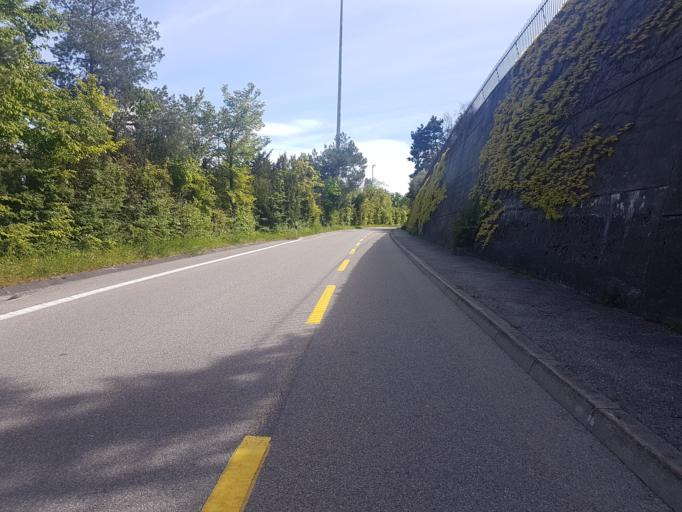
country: CH
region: Geneva
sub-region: Geneva
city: Bellevue
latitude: 46.2440
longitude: 6.1513
